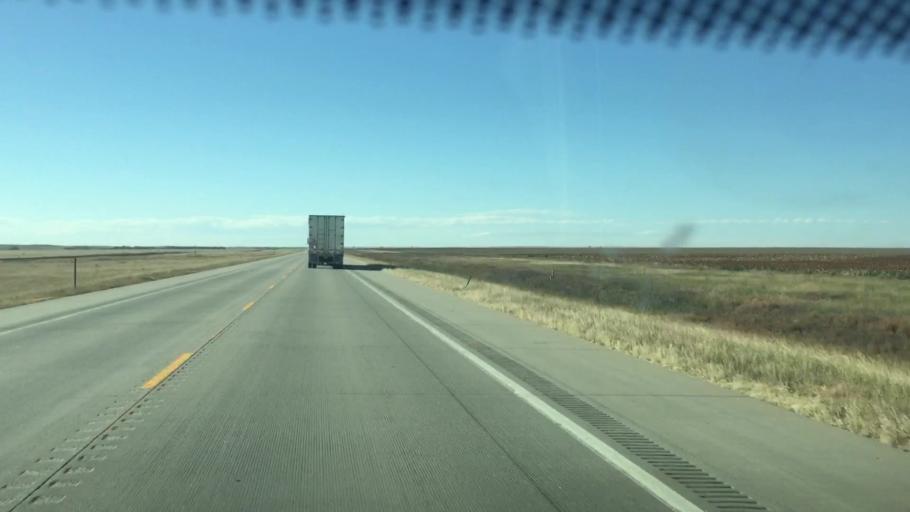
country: US
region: Colorado
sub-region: Kiowa County
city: Eads
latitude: 38.7910
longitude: -102.9351
